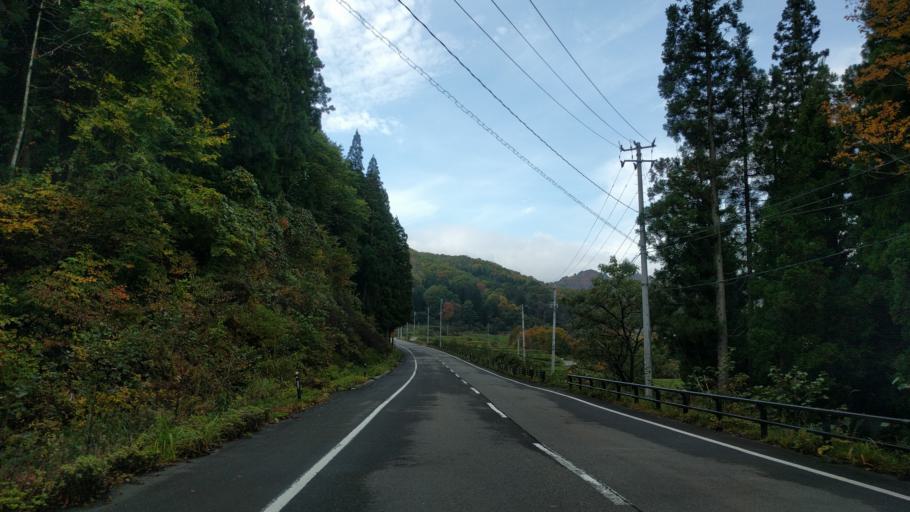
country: JP
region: Fukushima
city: Kitakata
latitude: 37.3982
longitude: 139.6948
